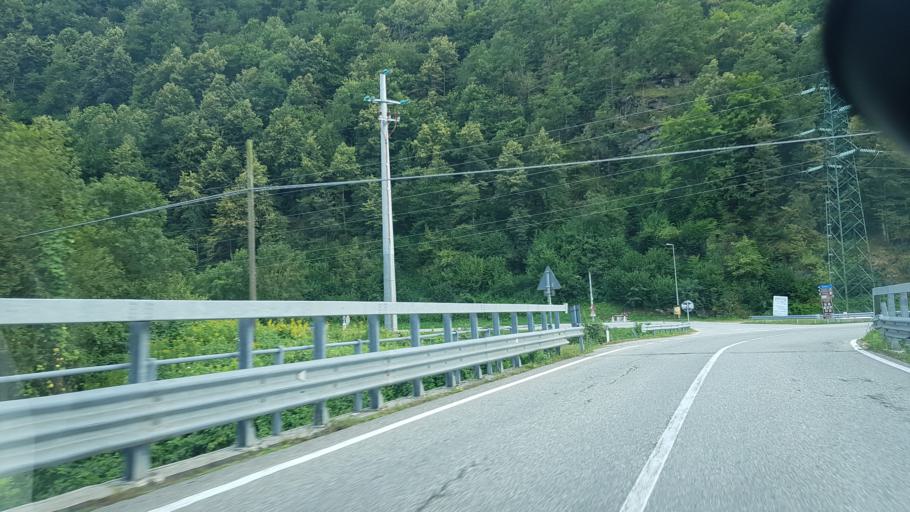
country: IT
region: Piedmont
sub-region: Provincia di Cuneo
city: Valmala
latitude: 44.5562
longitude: 7.3357
